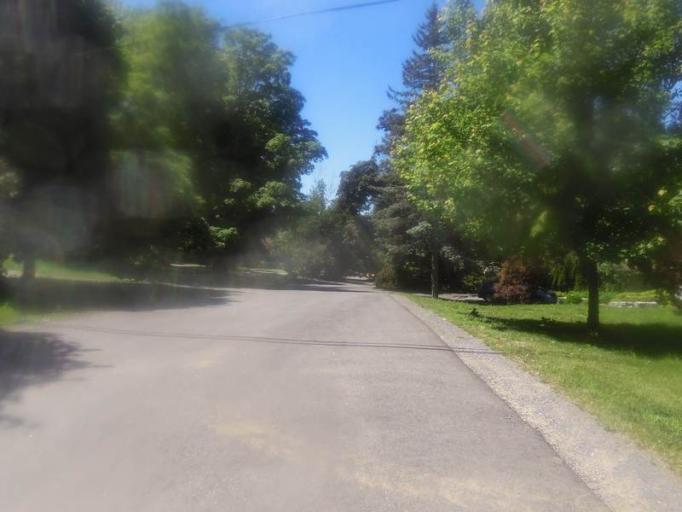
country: CA
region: Ontario
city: Kingston
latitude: 44.2427
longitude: -76.5328
